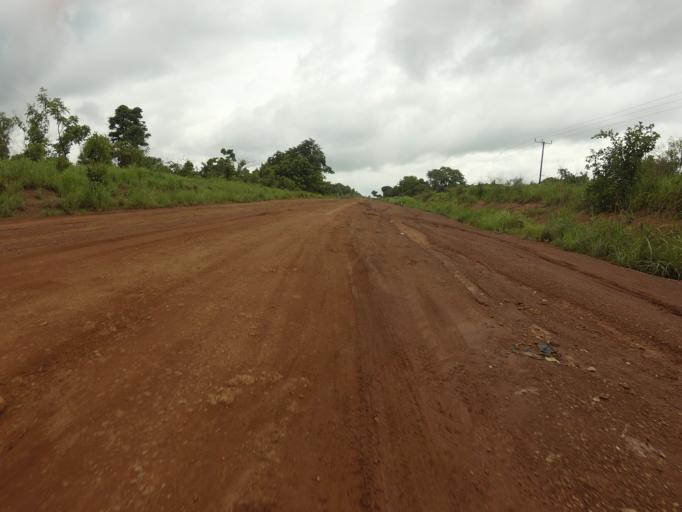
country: GH
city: Kpandae
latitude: 8.3149
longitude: 0.4796
